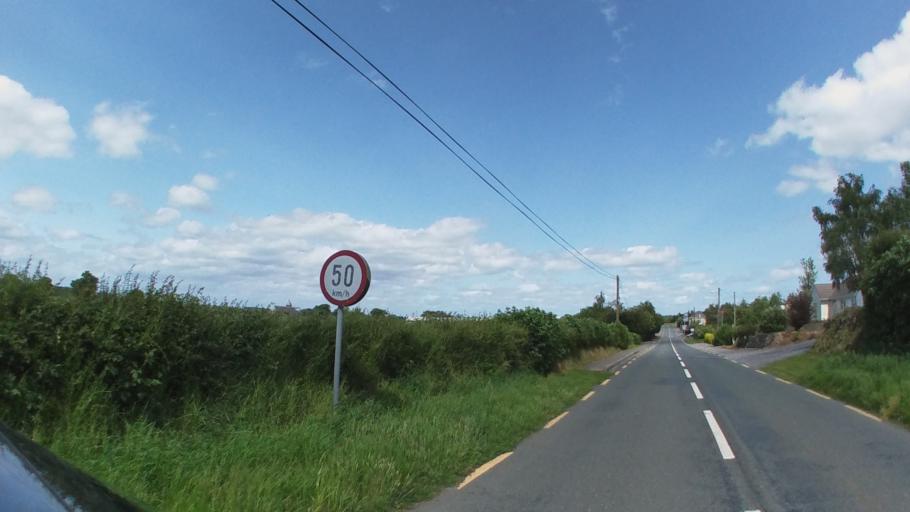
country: IE
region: Leinster
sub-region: Kildare
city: Moone
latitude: 53.0161
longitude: -6.8030
